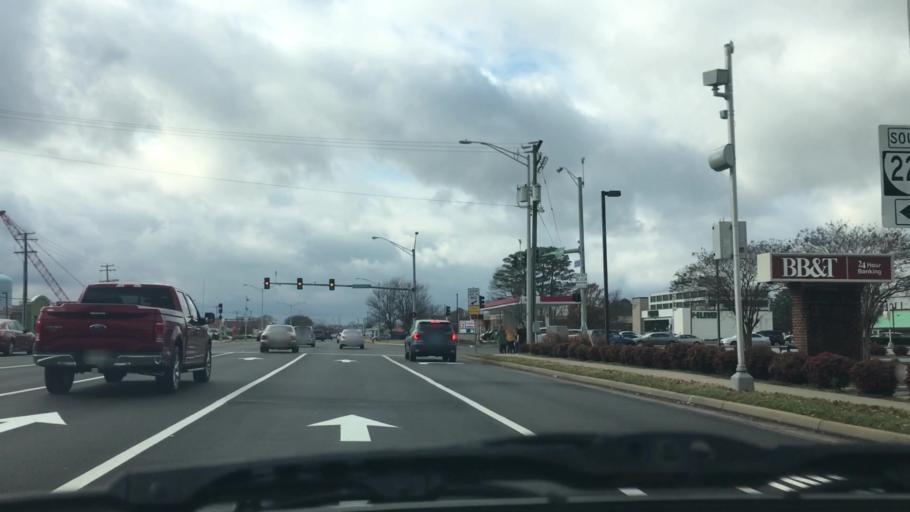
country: US
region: Virginia
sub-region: City of Chesapeake
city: Chesapeake
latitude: 36.8438
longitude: -76.1368
